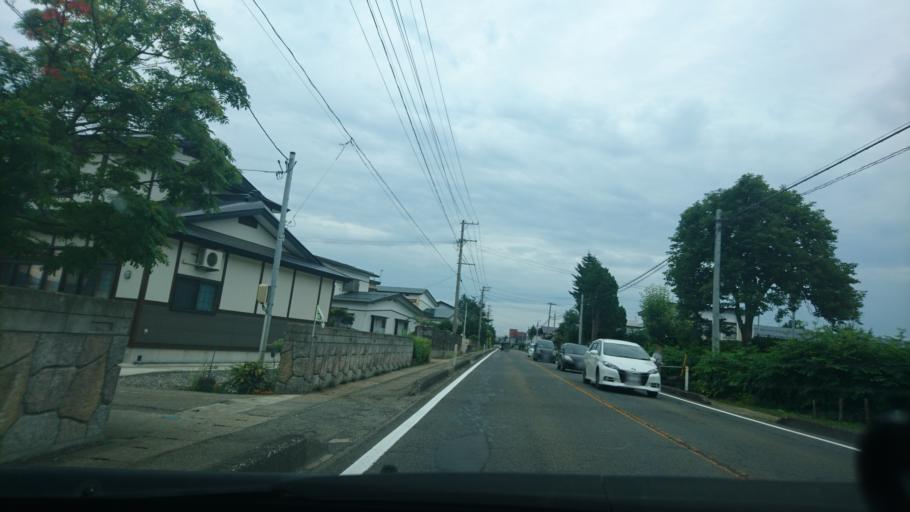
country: JP
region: Akita
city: Yokotemachi
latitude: 39.3967
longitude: 140.5647
